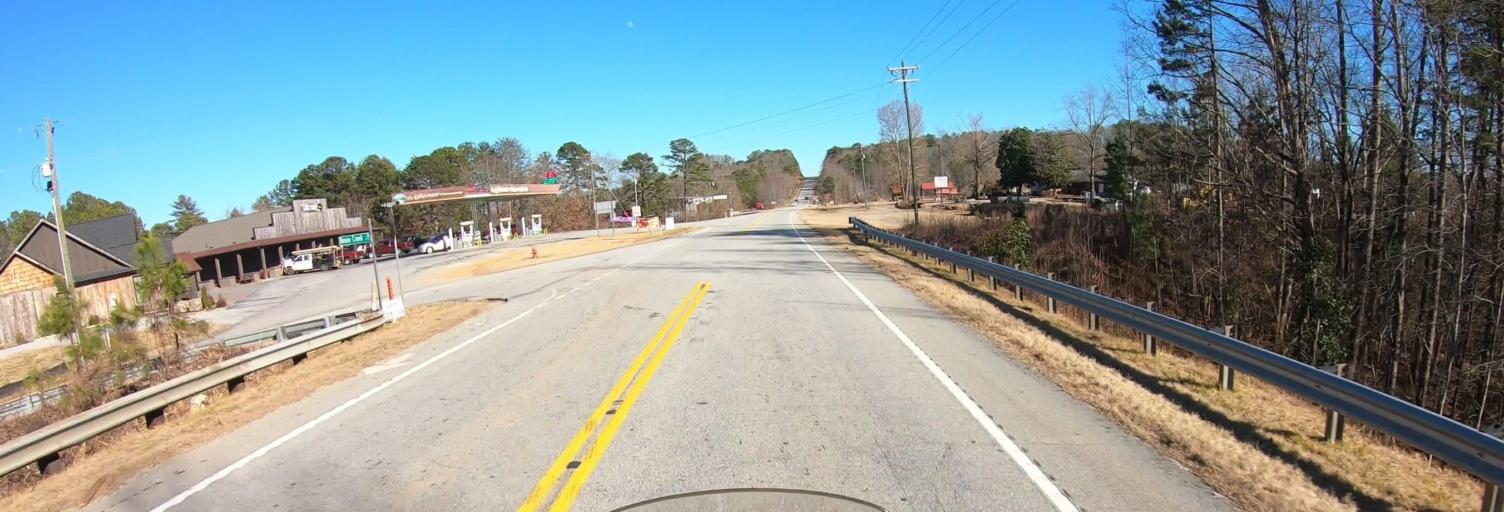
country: US
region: South Carolina
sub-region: Oconee County
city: Walhalla
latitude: 34.9127
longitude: -82.9369
